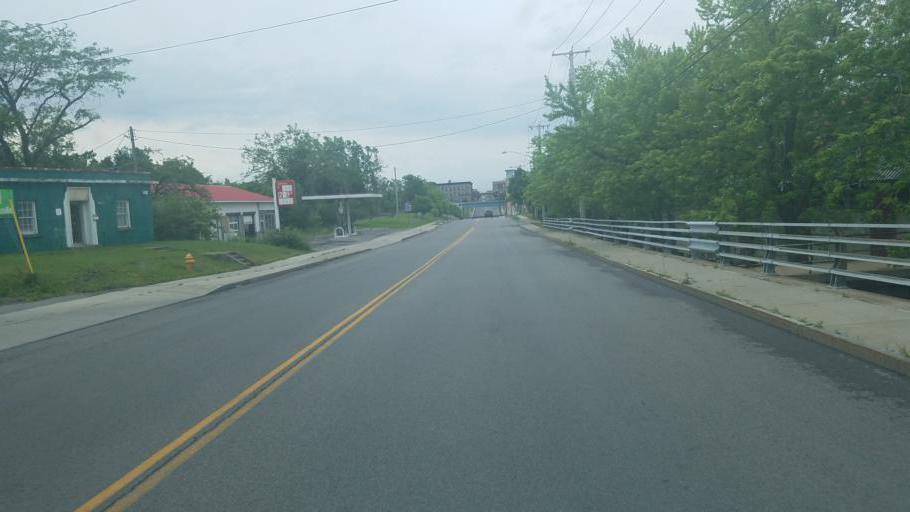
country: CA
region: Ontario
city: Niagara Falls
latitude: 43.1128
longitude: -79.0554
